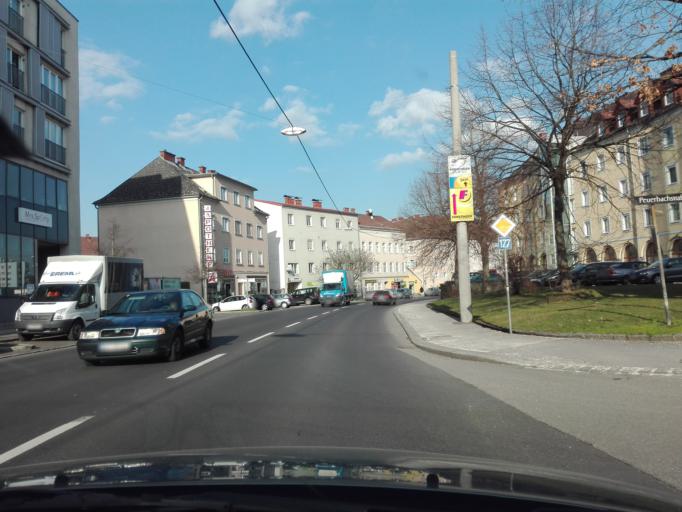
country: AT
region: Upper Austria
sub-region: Linz Stadt
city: Linz
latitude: 48.3179
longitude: 14.2838
